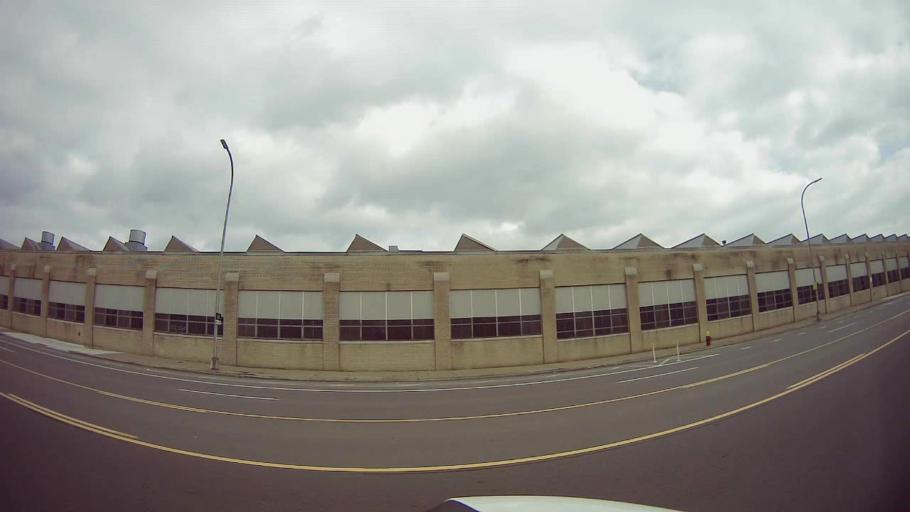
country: US
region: Michigan
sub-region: Wayne County
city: Dearborn
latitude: 42.3481
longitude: -83.1330
